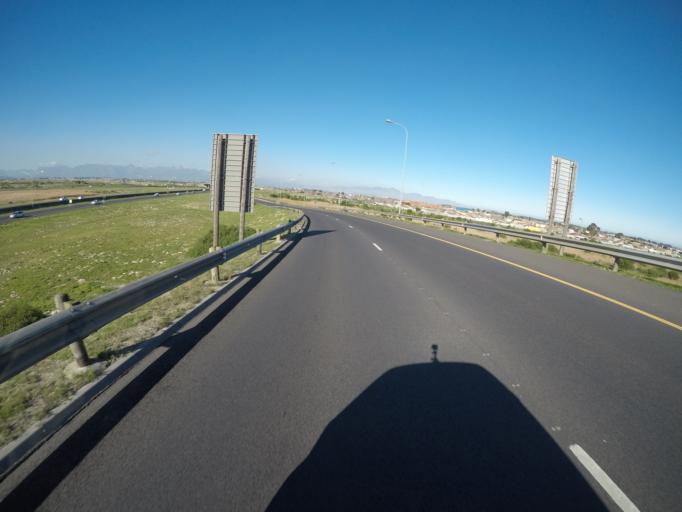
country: ZA
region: Western Cape
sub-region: City of Cape Town
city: Lansdowne
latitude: -34.0025
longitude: 18.6340
